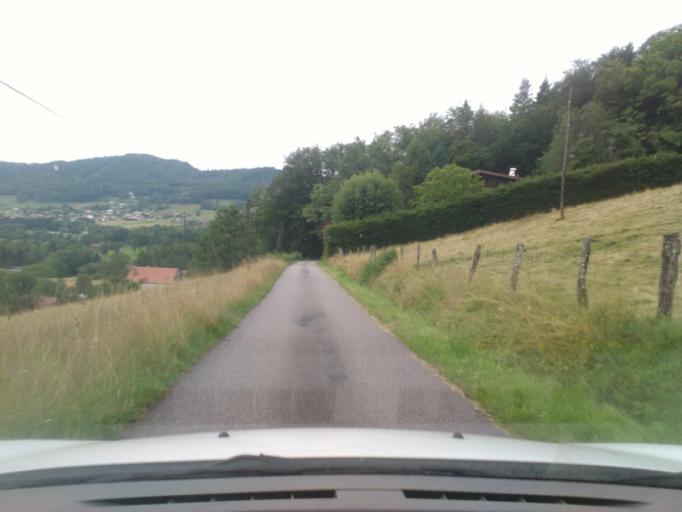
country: FR
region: Lorraine
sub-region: Departement des Vosges
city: Le Tholy
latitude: 48.1248
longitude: 6.6847
